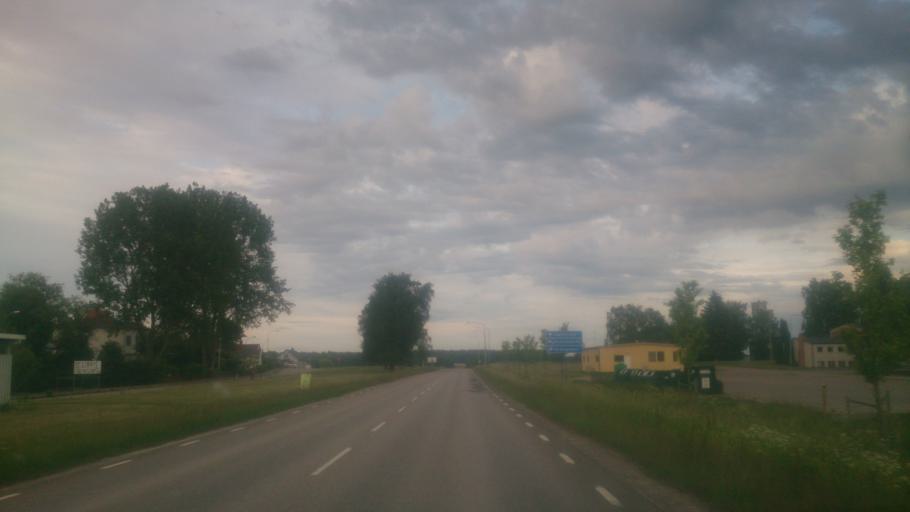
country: SE
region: OEstergoetland
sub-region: Motala Kommun
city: Borensberg
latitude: 58.4783
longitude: 15.2280
